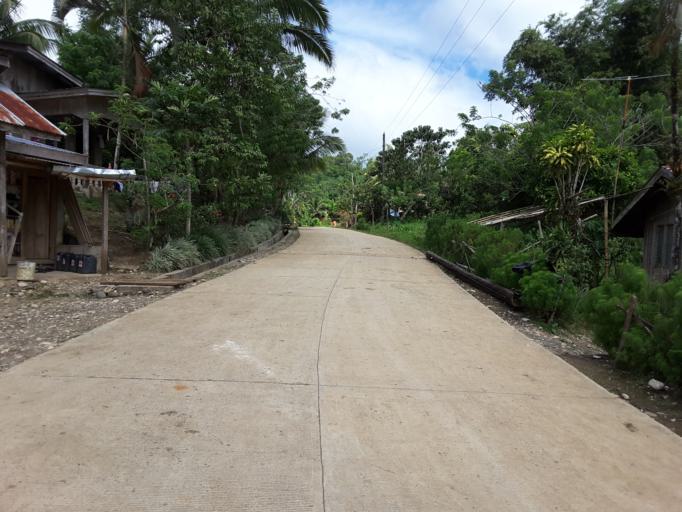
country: PH
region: Caraga
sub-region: Province of Agusan del Sur
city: Bayugan
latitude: 8.7828
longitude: 125.8275
